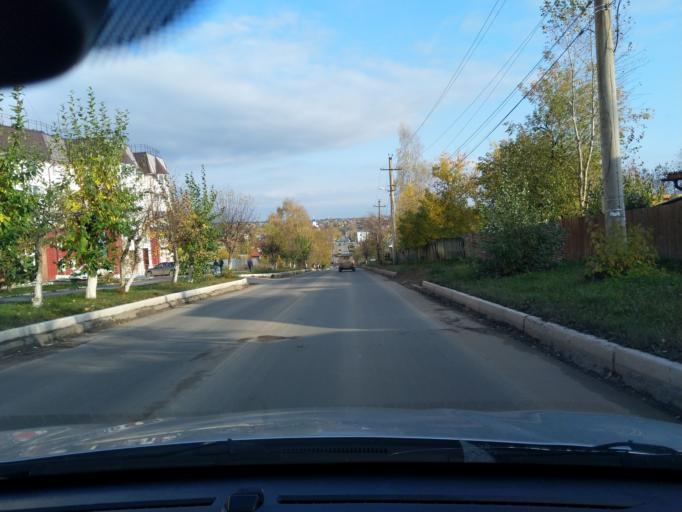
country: RU
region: Perm
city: Dobryanka
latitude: 58.4621
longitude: 56.4046
